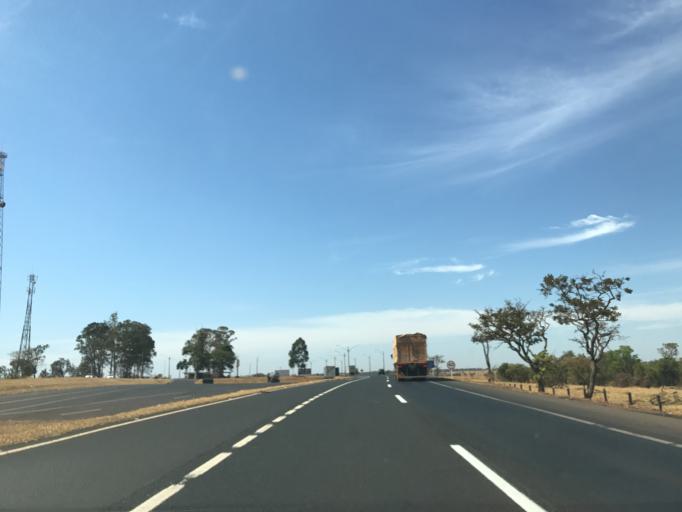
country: BR
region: Minas Gerais
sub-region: Monte Alegre De Minas
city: Monte Alegre de Minas
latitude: -18.8658
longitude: -49.0690
